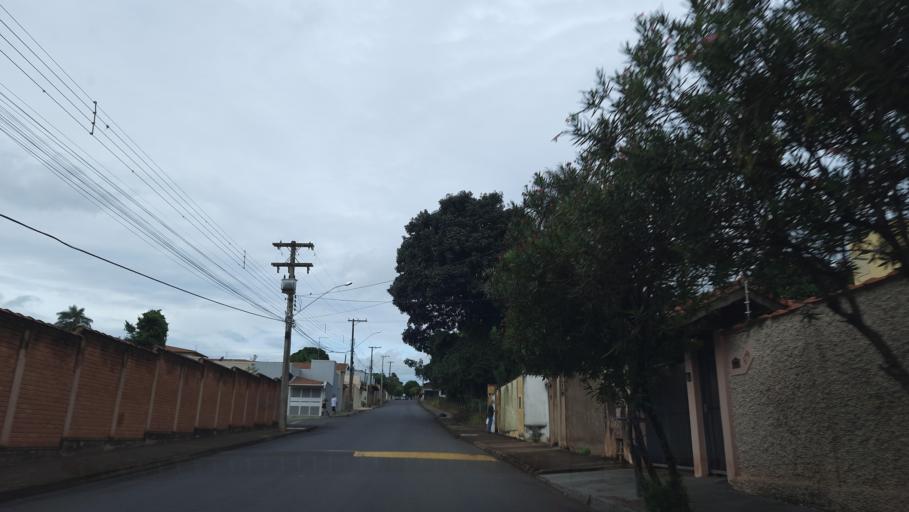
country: BR
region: Sao Paulo
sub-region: Casa Branca
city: Casa Branca
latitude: -21.7811
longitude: -47.0868
